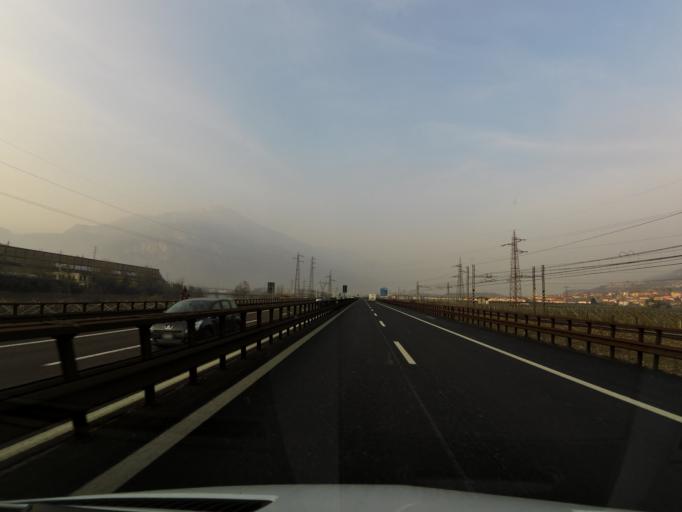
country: IT
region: Trentino-Alto Adige
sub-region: Provincia di Trento
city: Marco
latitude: 45.8352
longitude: 11.0029
